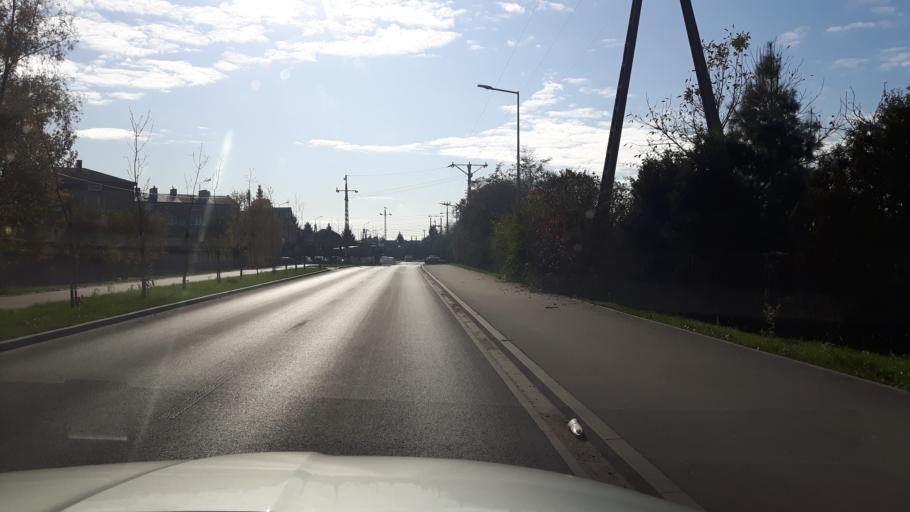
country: PL
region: Masovian Voivodeship
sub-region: Powiat wolominski
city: Zabki
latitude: 52.2938
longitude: 21.1001
